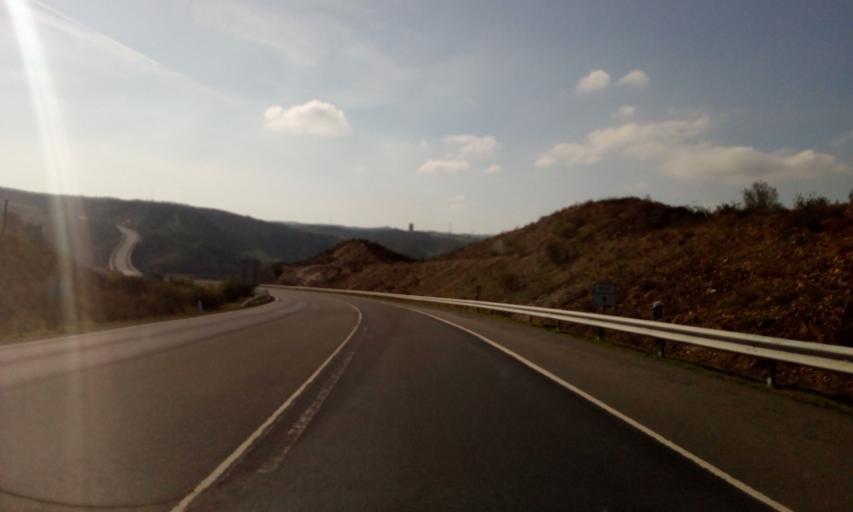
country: PT
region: Faro
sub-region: Castro Marim
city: Castro Marim
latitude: 37.2804
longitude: -7.4935
